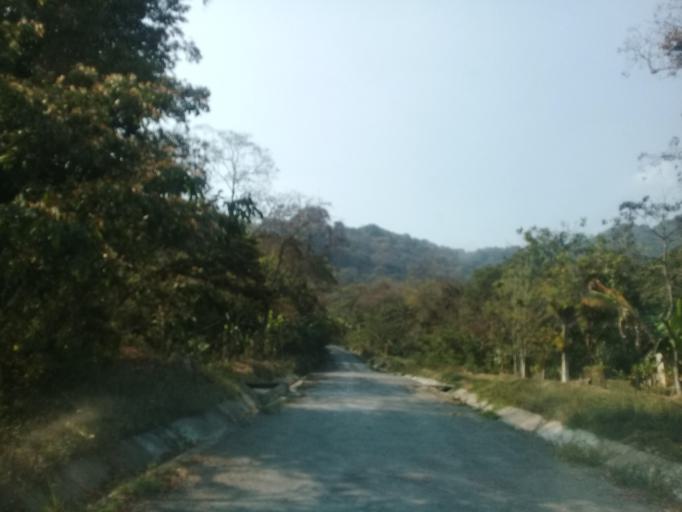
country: MX
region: Veracruz
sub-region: Ixtaczoquitlan
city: Campo Chico
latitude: 18.8405
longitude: -97.0304
